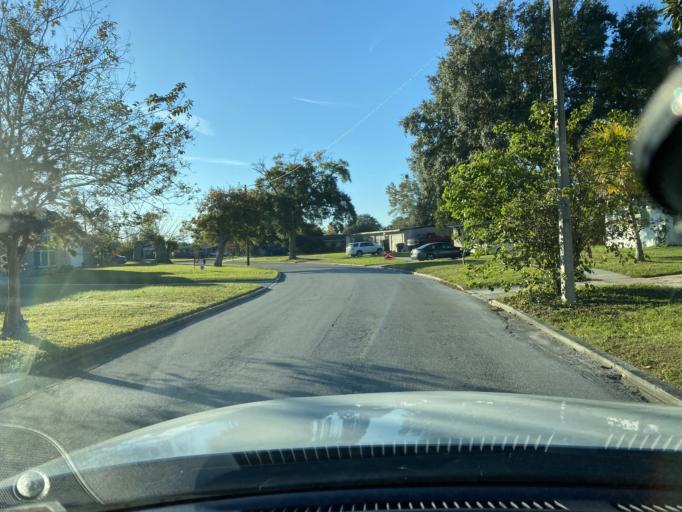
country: US
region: Florida
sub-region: Orange County
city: Azalea Park
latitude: 28.5344
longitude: -81.3023
